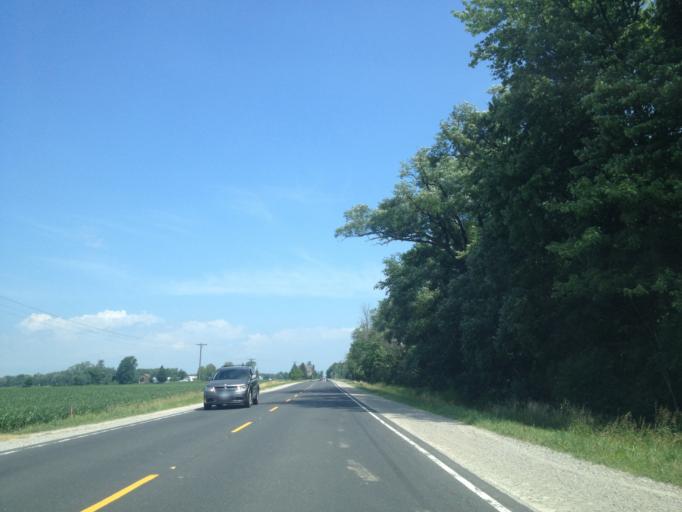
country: CA
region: Ontario
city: Stratford
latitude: 43.3373
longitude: -81.2062
